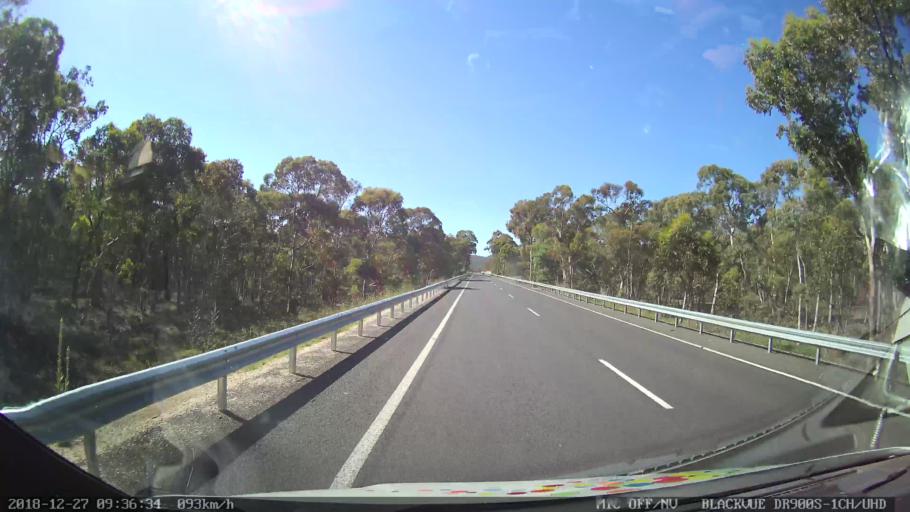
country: AU
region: New South Wales
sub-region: Lithgow
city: Portland
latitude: -33.2539
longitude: 150.0358
